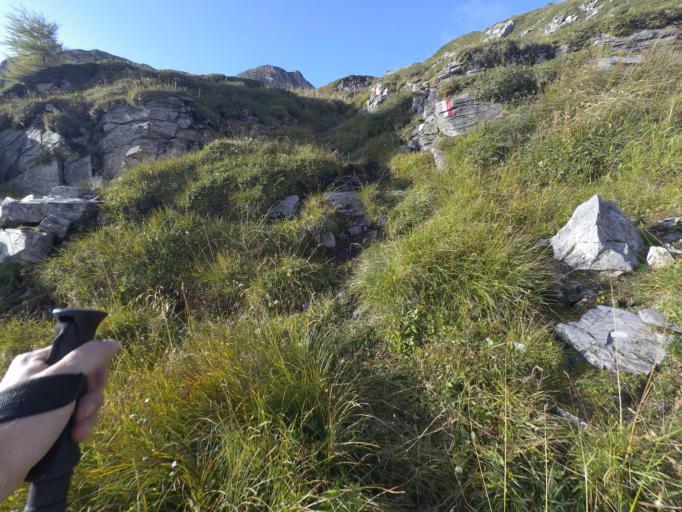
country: AT
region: Salzburg
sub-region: Politischer Bezirk Sankt Johann im Pongau
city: Untertauern
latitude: 47.2267
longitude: 13.4255
